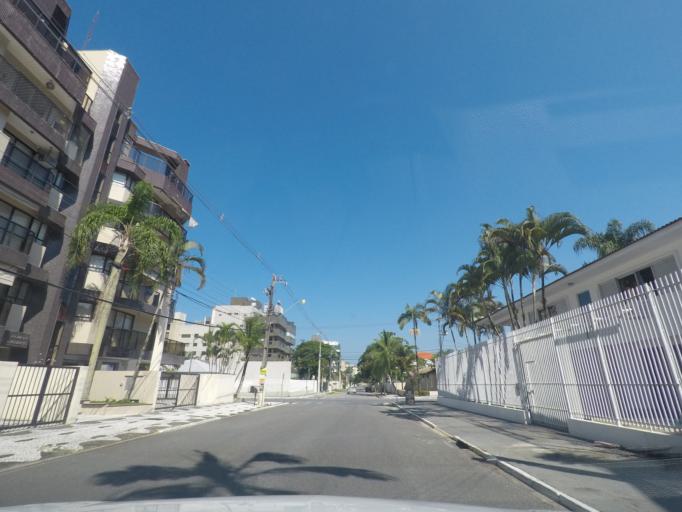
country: BR
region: Parana
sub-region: Guaratuba
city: Guaratuba
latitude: -25.8417
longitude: -48.5412
